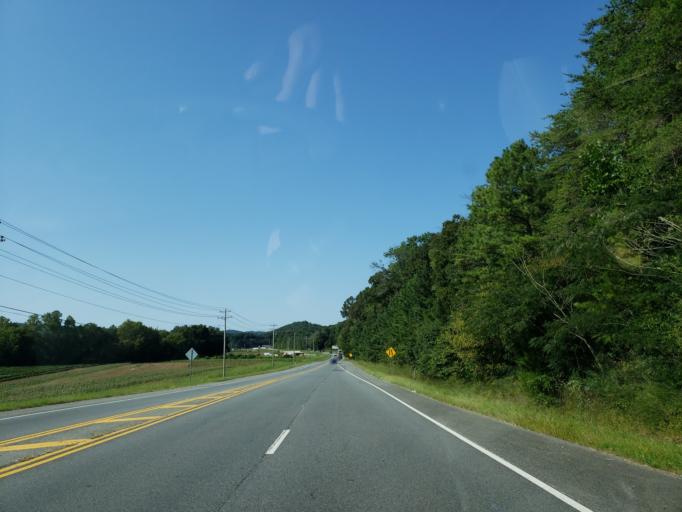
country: US
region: Georgia
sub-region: Catoosa County
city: Ringgold
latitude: 34.8972
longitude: -85.0756
